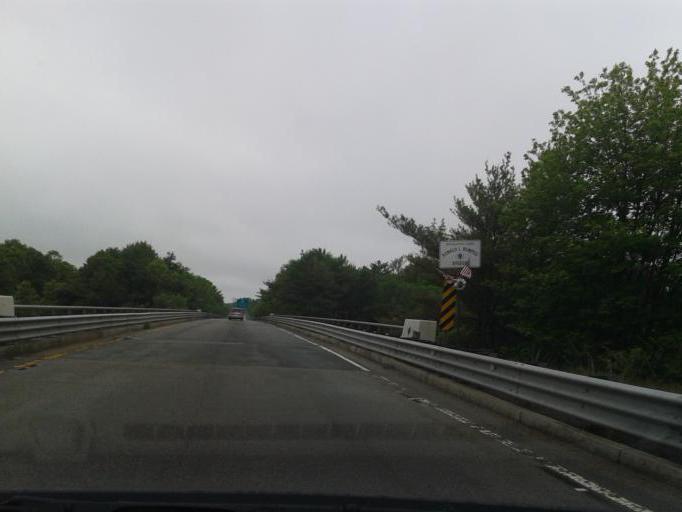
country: US
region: Massachusetts
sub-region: Plymouth County
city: Wareham Center
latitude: 41.7845
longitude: -70.7322
